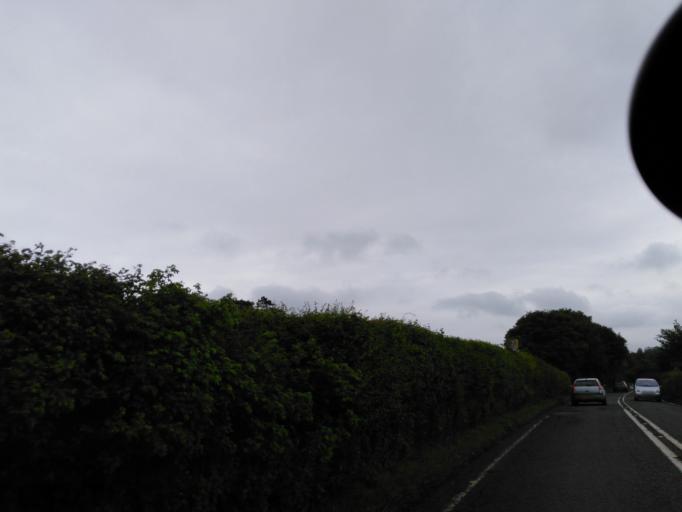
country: GB
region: England
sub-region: Somerset
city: Street
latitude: 51.1219
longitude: -2.7903
